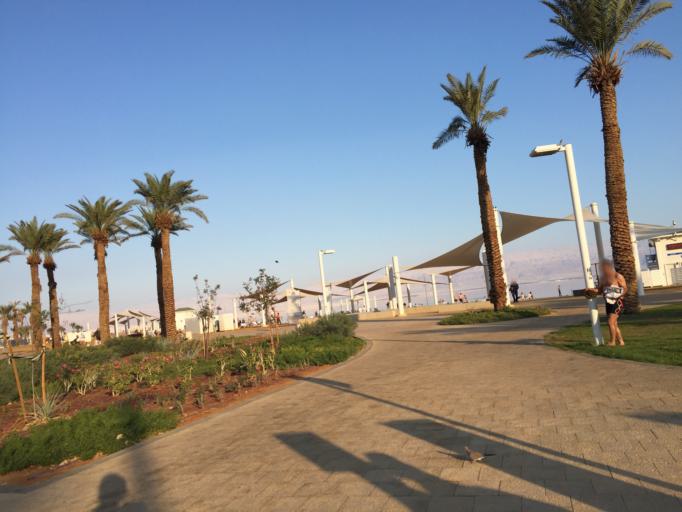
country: IL
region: Southern District
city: `En Boqeq
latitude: 31.1962
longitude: 35.3625
